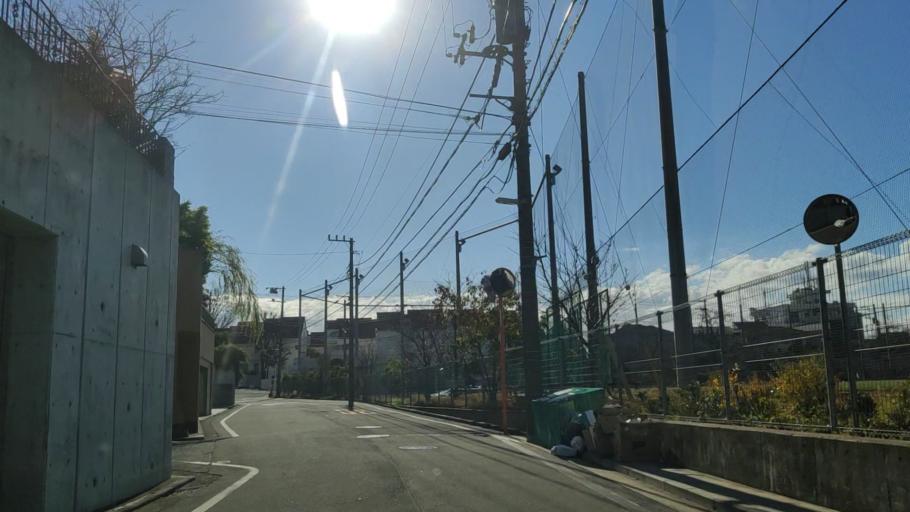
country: JP
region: Kanagawa
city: Yokohama
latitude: 35.4216
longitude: 139.6430
